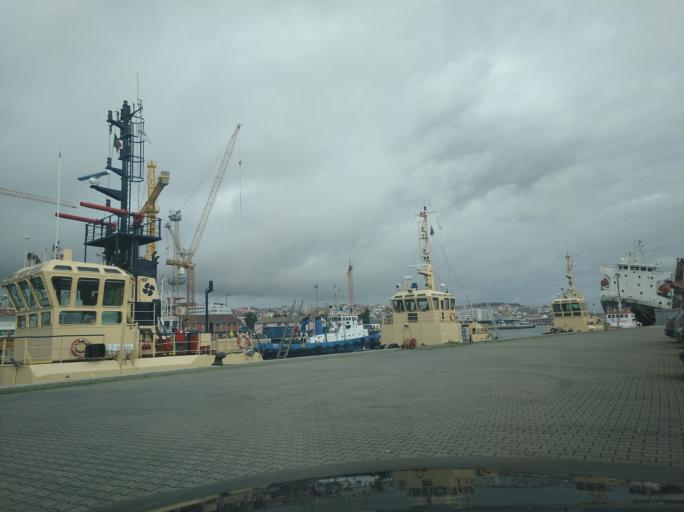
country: PT
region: Setubal
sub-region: Almada
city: Cacilhas
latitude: 38.7017
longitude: -9.1607
